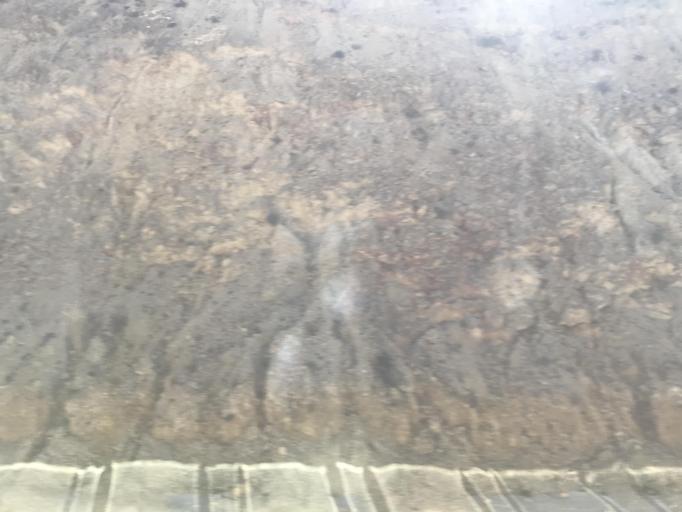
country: ES
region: Castille-La Mancha
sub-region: Provincia de Guadalajara
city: Anguita
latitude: 41.1085
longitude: -2.3672
